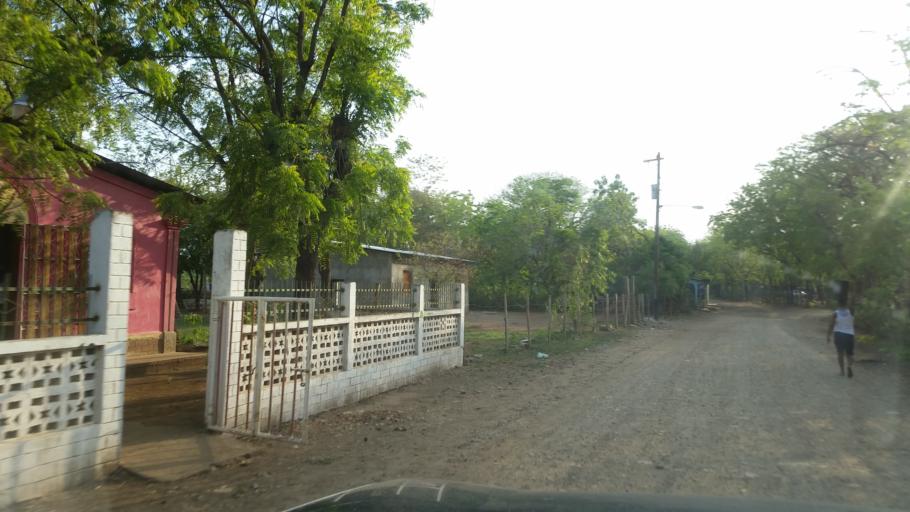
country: NI
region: Managua
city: Masachapa
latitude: 11.7973
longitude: -86.4706
